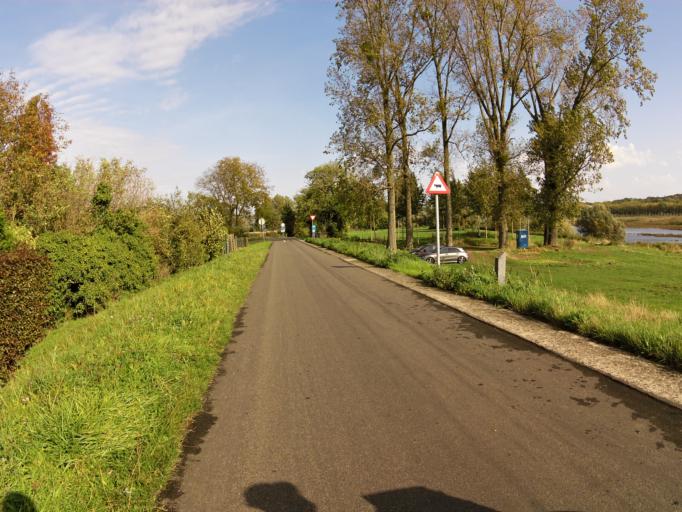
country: NL
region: Limburg
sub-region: Gemeente Stein
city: Elsloo
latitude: 50.9308
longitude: 5.7323
